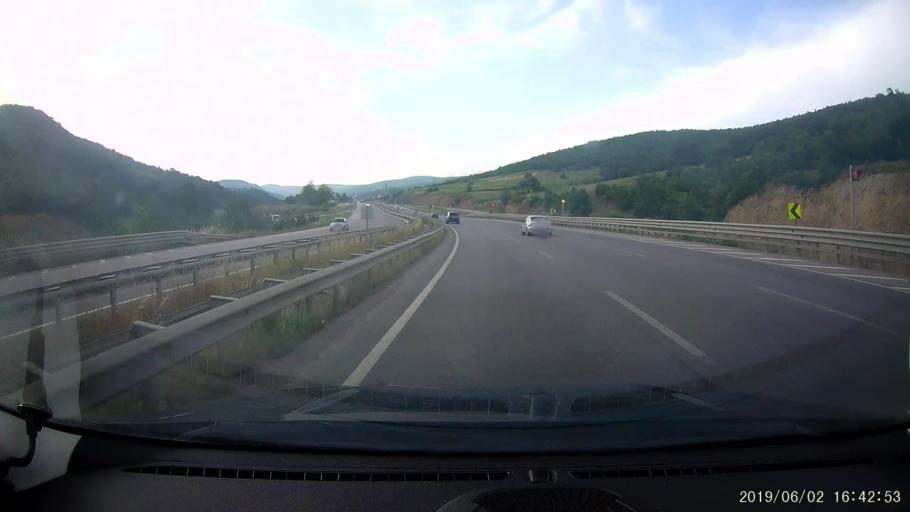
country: TR
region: Samsun
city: Kavak
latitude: 41.1257
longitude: 36.1379
